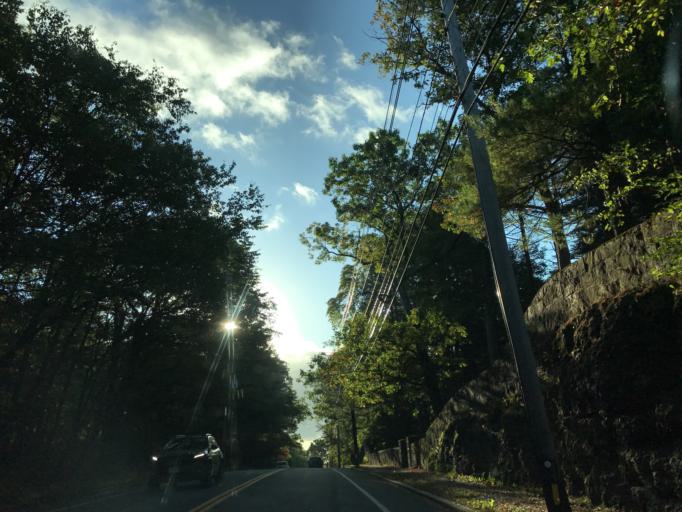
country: US
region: Massachusetts
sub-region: Suffolk County
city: Jamaica Plain
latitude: 42.3039
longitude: -71.1437
